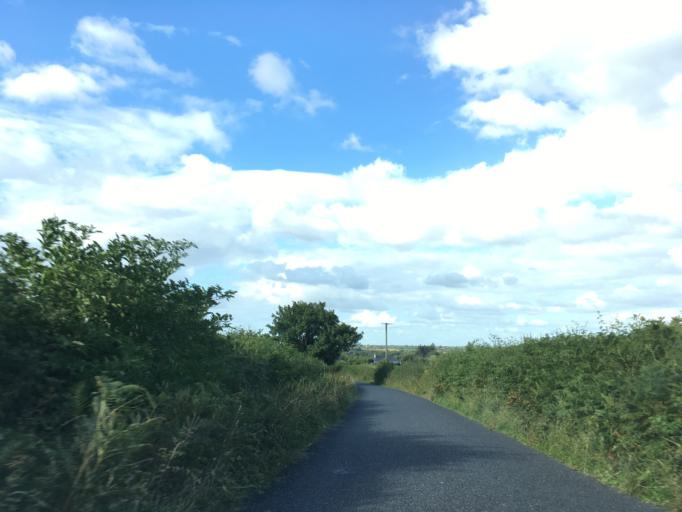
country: IE
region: Munster
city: Cahir
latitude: 52.2684
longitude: -7.9574
